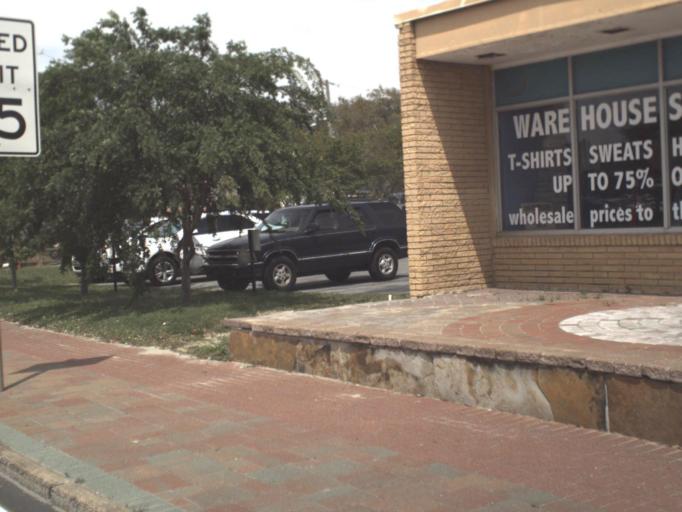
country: US
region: Florida
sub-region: Okaloosa County
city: Fort Walton Beach
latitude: 30.4218
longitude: -86.6098
